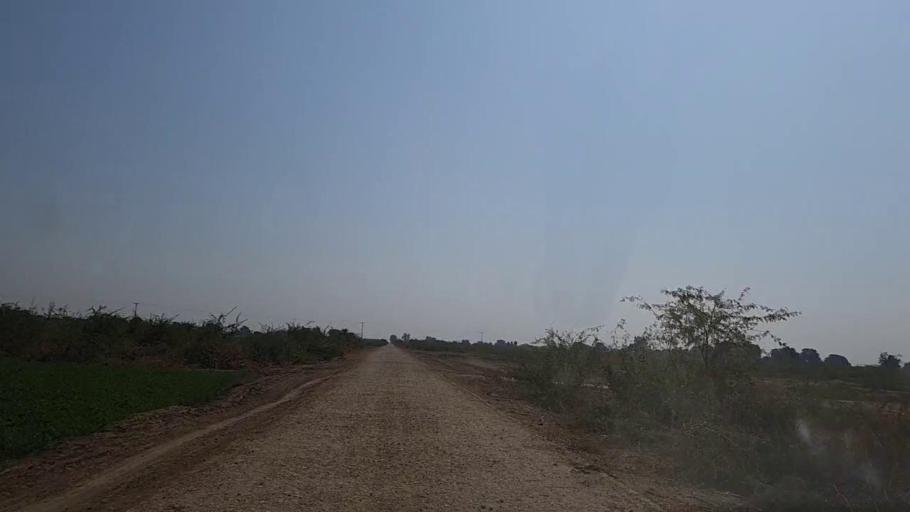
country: PK
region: Sindh
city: Digri
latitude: 24.9786
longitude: 69.2057
